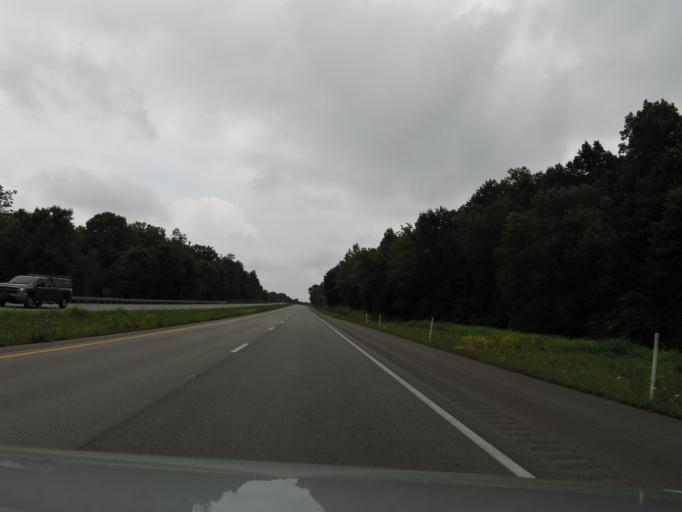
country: US
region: Kentucky
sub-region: Grayson County
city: Leitchfield
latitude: 37.4264
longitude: -86.3881
